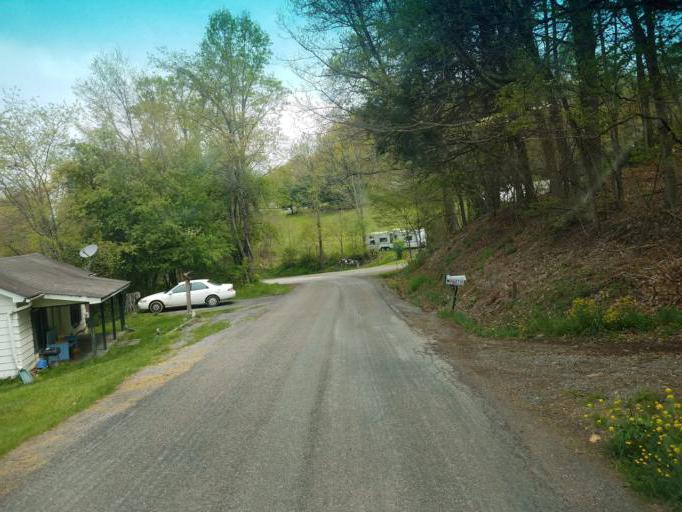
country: US
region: Virginia
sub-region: Smyth County
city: Marion
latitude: 36.8043
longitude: -81.4637
